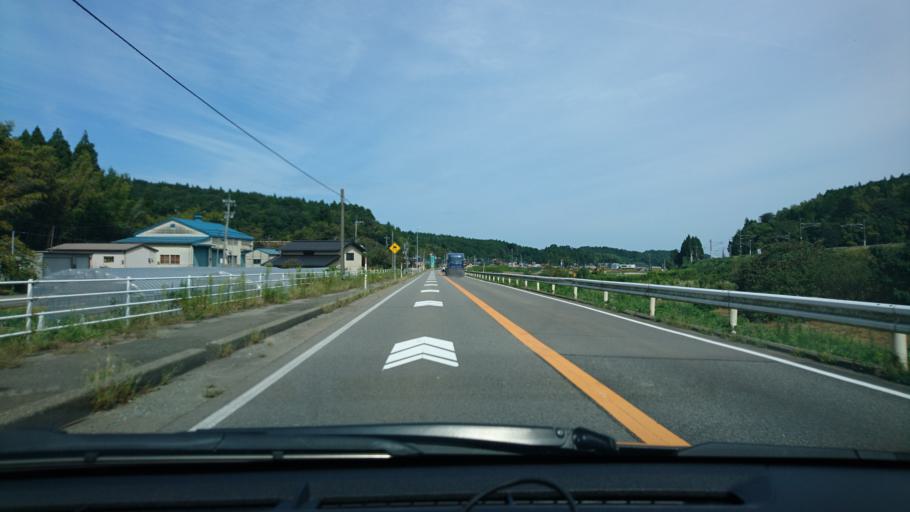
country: JP
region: Fukui
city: Maruoka
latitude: 36.2832
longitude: 136.2934
